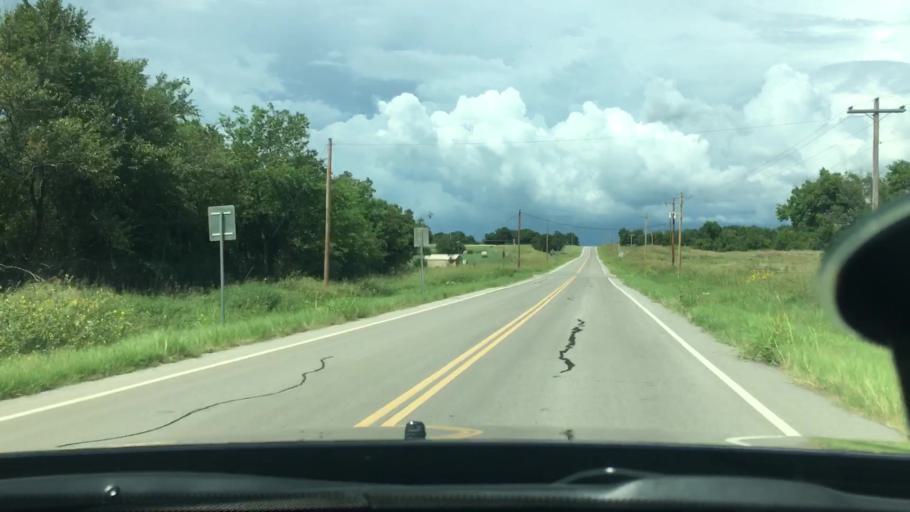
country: US
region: Oklahoma
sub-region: Garvin County
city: Stratford
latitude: 34.8246
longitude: -97.0554
